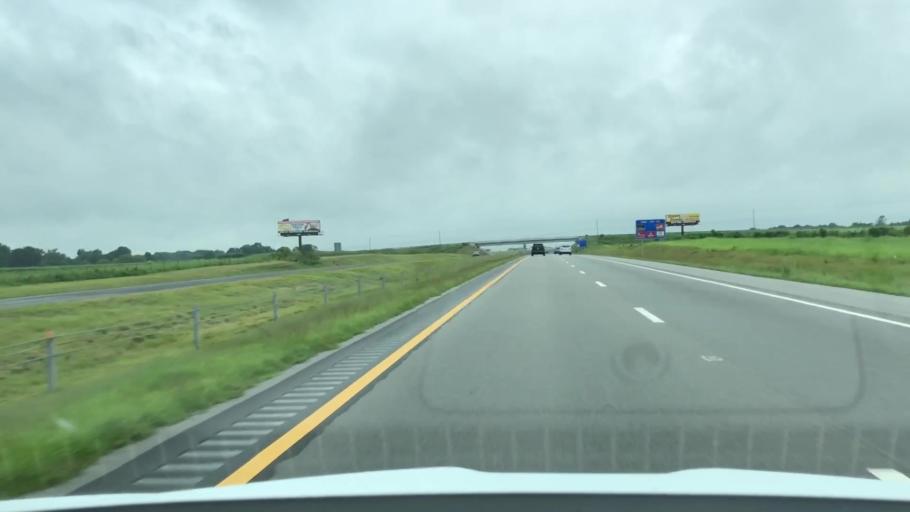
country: US
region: North Carolina
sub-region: Wayne County
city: Elroy
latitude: 35.4066
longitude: -77.8849
